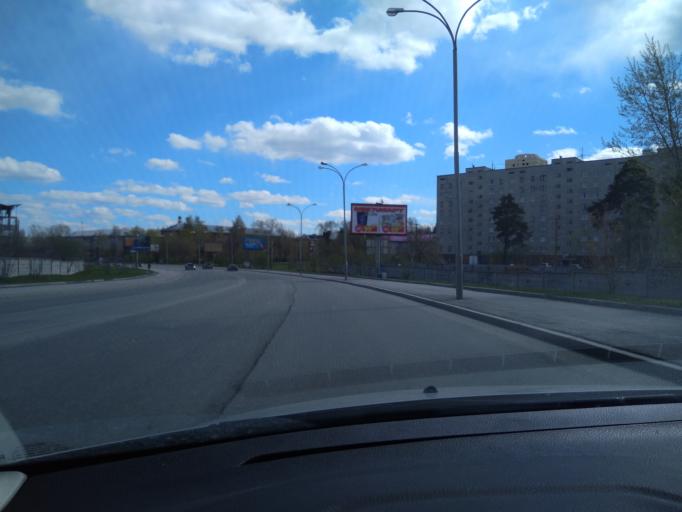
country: RU
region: Sverdlovsk
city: Shuvakish
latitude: 56.8765
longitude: 60.5258
